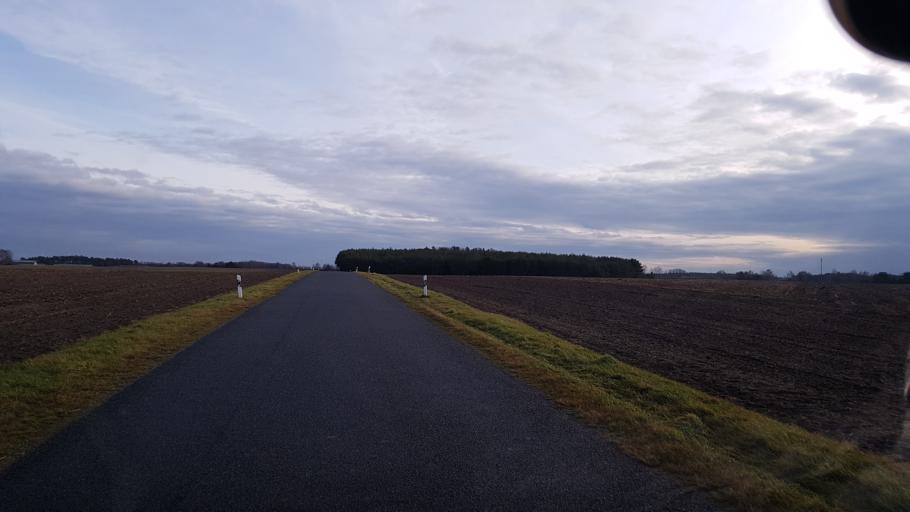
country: DE
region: Brandenburg
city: Bronkow
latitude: 51.6596
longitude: 13.8834
